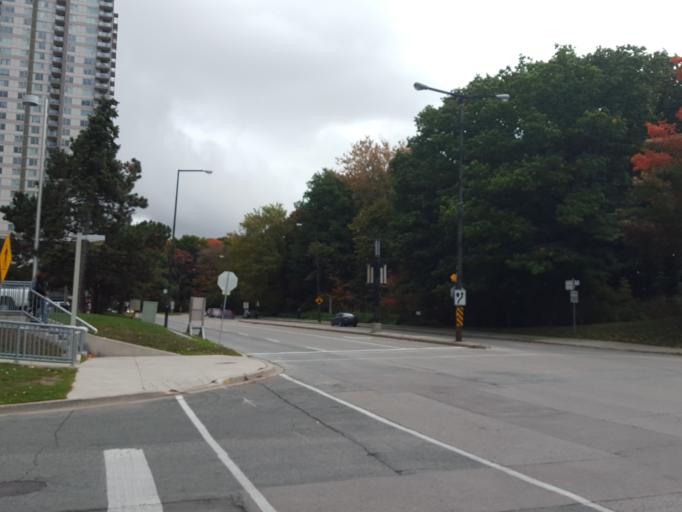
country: CA
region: Ontario
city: Scarborough
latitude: 43.7723
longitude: -79.2563
